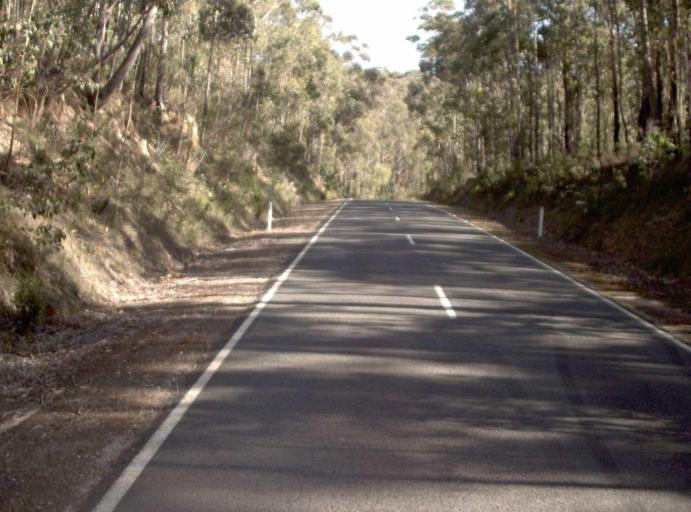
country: AU
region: Victoria
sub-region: East Gippsland
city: Lakes Entrance
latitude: -37.6545
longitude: 148.4776
